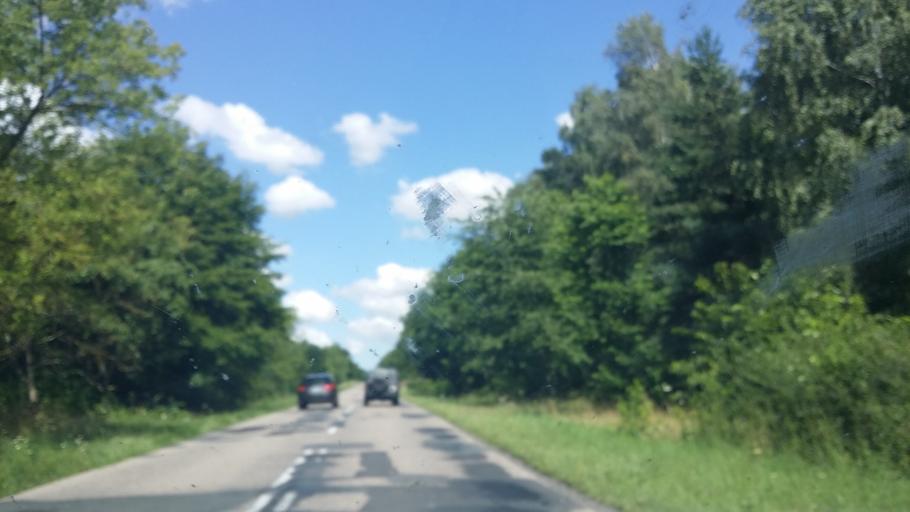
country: PL
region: West Pomeranian Voivodeship
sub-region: Powiat swidwinski
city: Slawoborze
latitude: 53.9122
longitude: 15.6895
